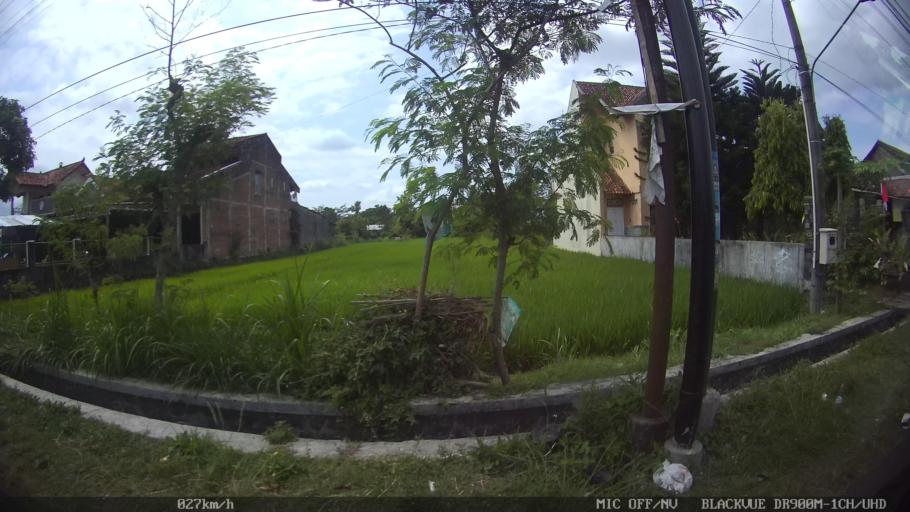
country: ID
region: Daerah Istimewa Yogyakarta
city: Depok
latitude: -7.7816
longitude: 110.4641
